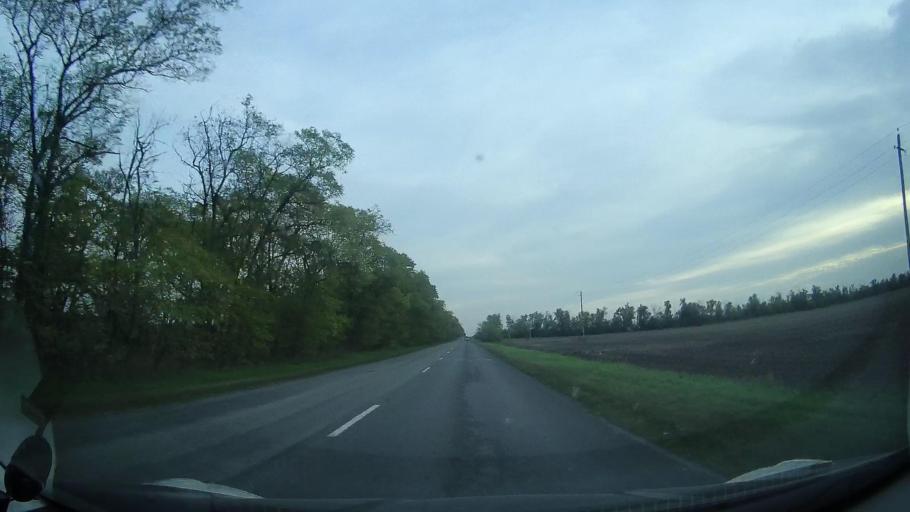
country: RU
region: Rostov
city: Ol'ginskaya
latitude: 47.1015
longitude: 39.9775
